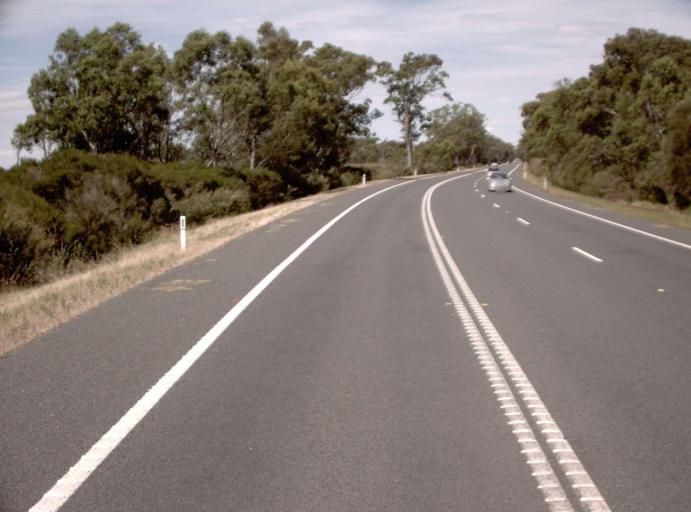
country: AU
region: Victoria
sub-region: Wellington
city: Sale
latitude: -37.9380
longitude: 147.1534
